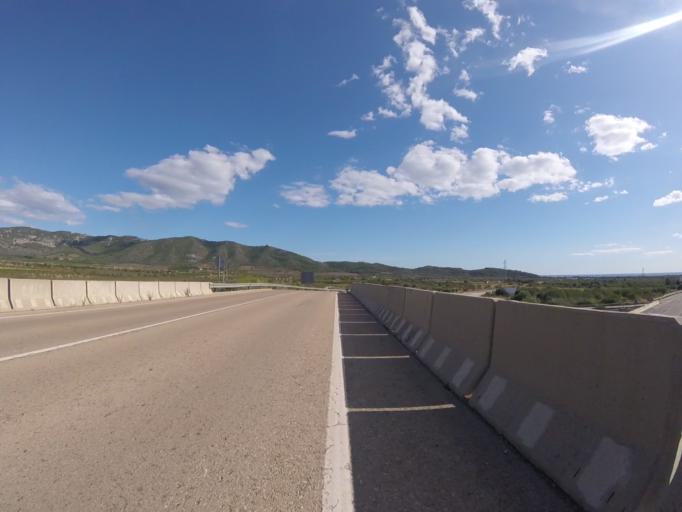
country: ES
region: Valencia
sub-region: Provincia de Castello
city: Alcala de Xivert
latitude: 40.2677
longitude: 0.2405
